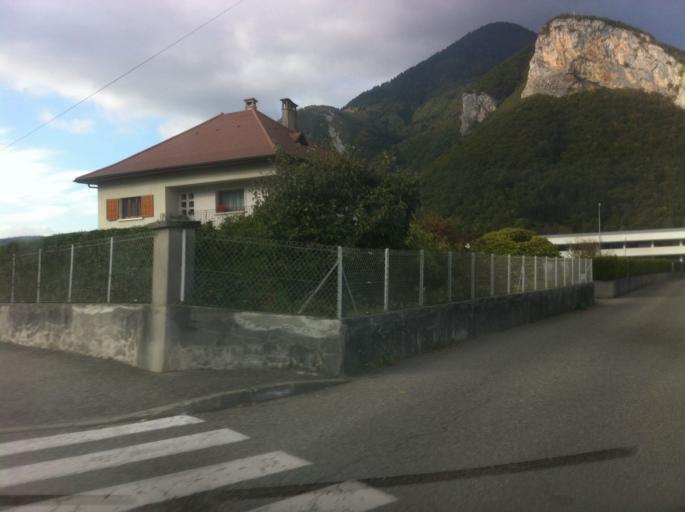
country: FR
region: Rhone-Alpes
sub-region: Departement de la Haute-Savoie
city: Faverges
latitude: 45.7491
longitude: 6.2904
